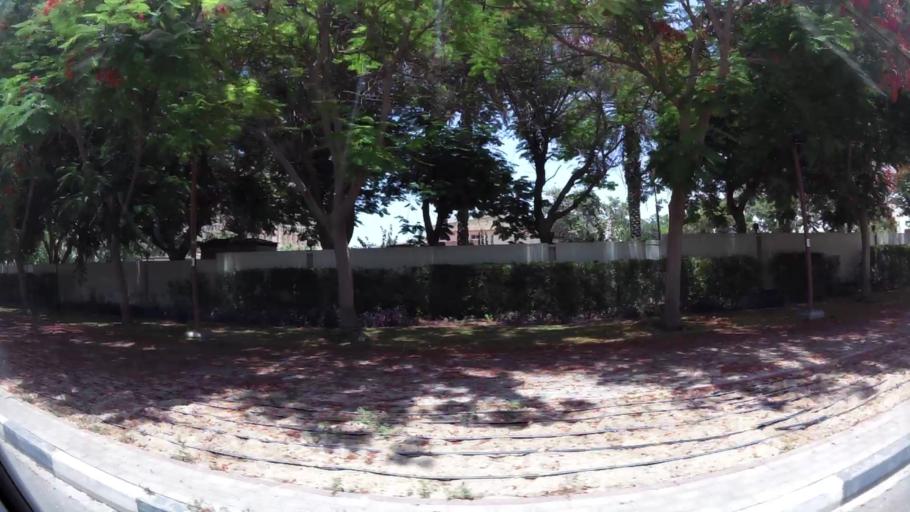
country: AE
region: Ash Shariqah
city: Sharjah
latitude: 25.2826
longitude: 55.3204
